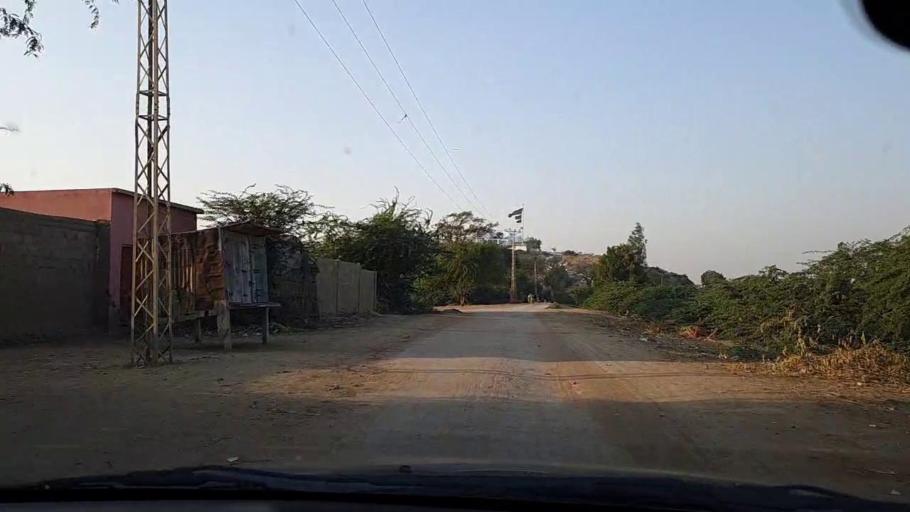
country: PK
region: Sindh
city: Thatta
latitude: 24.5591
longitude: 67.8809
